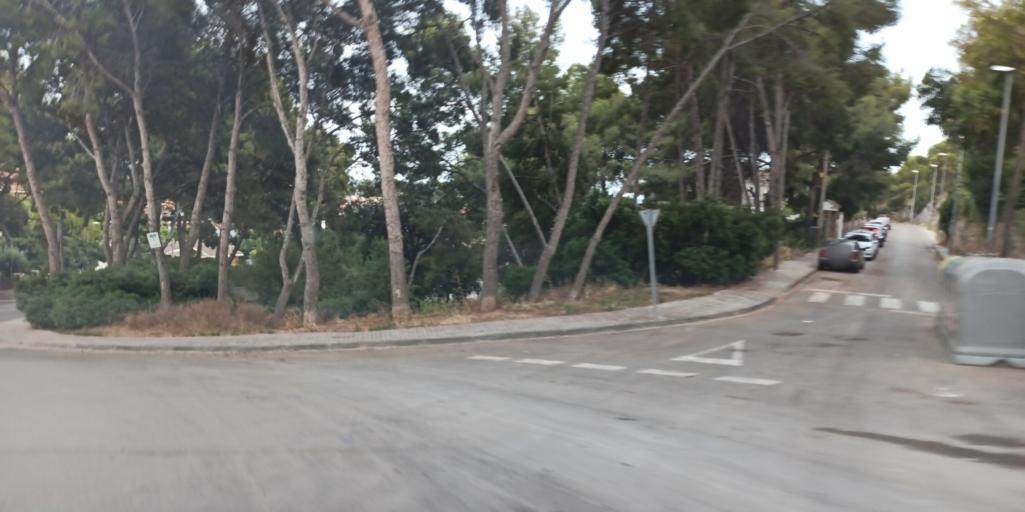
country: ES
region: Catalonia
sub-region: Provincia de Barcelona
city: Castelldefels
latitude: 41.2693
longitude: 1.9424
